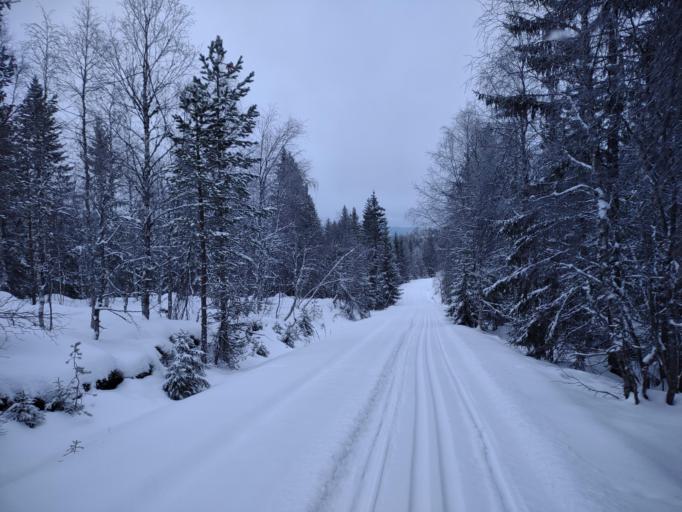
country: NO
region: Buskerud
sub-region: Flesberg
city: Lampeland
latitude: 59.7471
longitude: 9.4888
